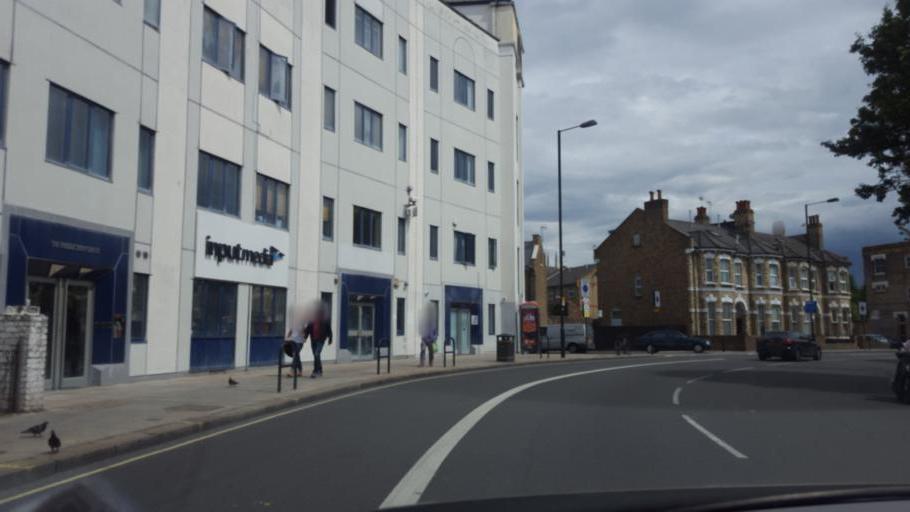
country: GB
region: England
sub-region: Greater London
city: Hammersmith
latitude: 51.5018
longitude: -0.2410
